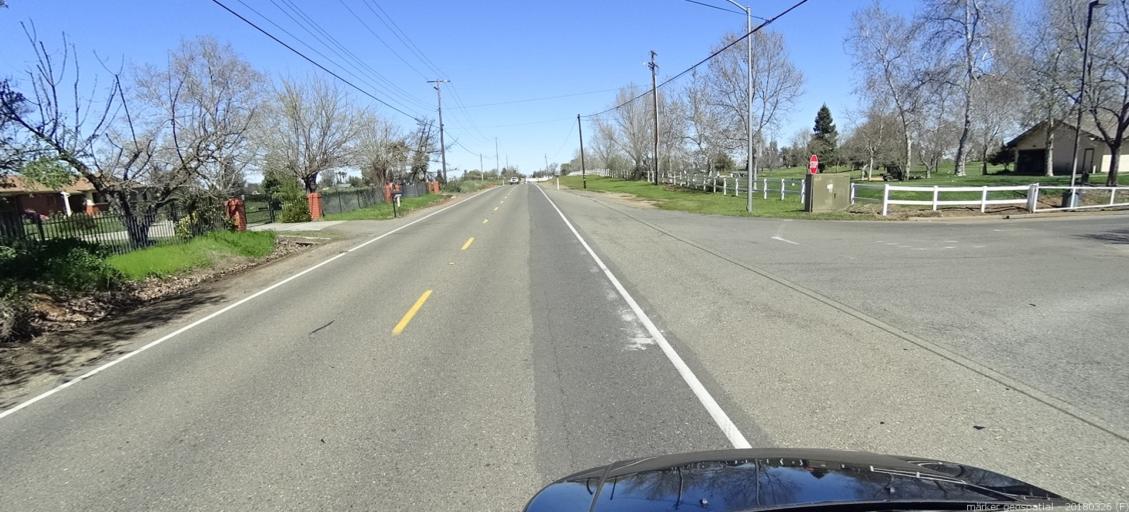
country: US
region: California
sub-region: Sacramento County
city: Vineyard
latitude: 38.4774
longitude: -121.3161
